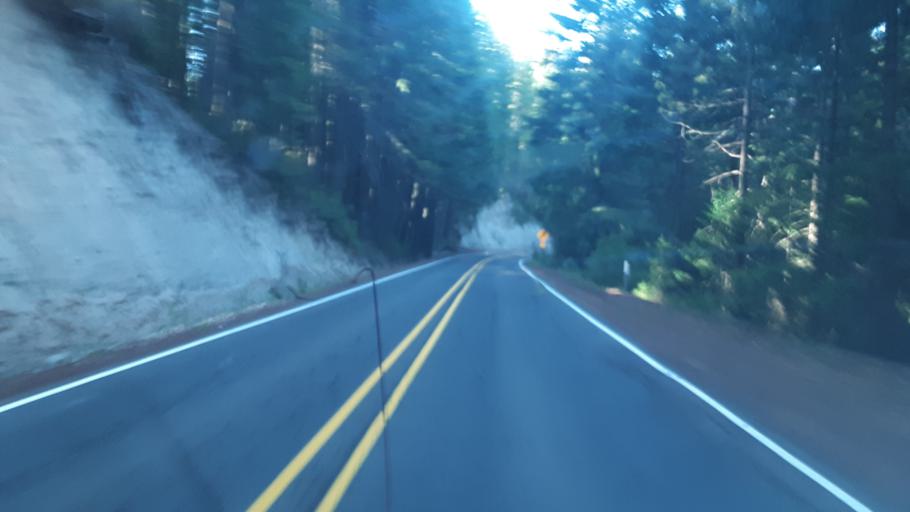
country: US
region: Oregon
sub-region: Jackson County
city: Shady Cove
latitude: 42.9378
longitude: -122.4198
